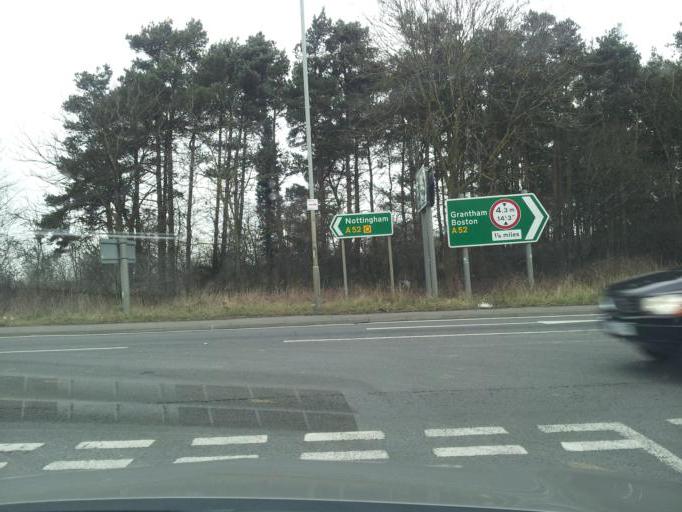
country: GB
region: England
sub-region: Lincolnshire
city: Barrowby
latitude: 52.9195
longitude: -0.6844
